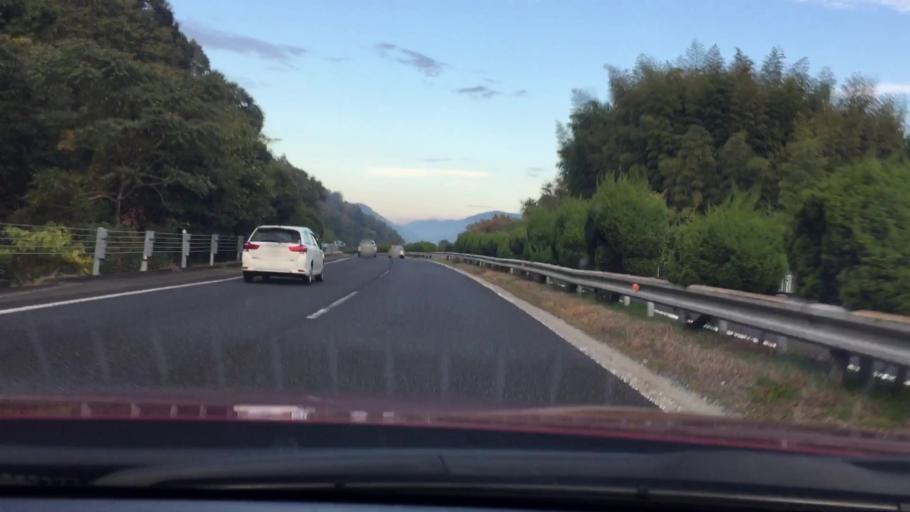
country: JP
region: Hyogo
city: Himeji
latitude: 34.9599
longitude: 134.7042
